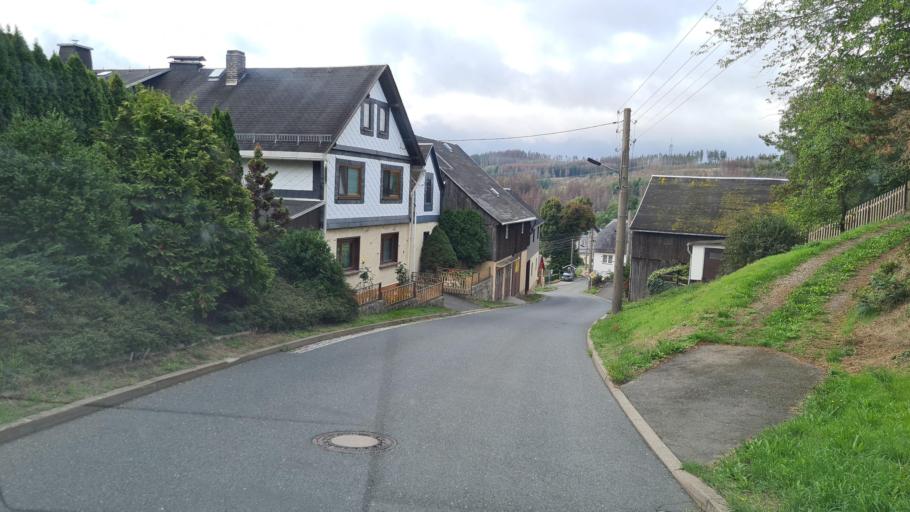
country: DE
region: Thuringia
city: Leutenberg
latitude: 50.5641
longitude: 11.4240
